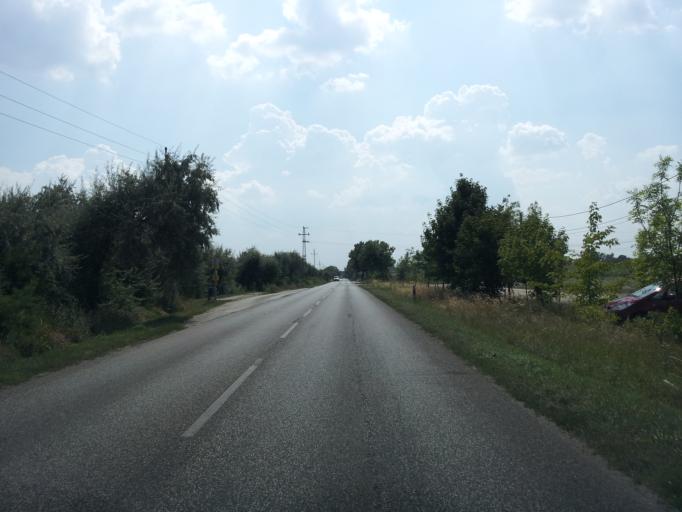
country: HU
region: Pest
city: Taksony
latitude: 47.3210
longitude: 19.0489
